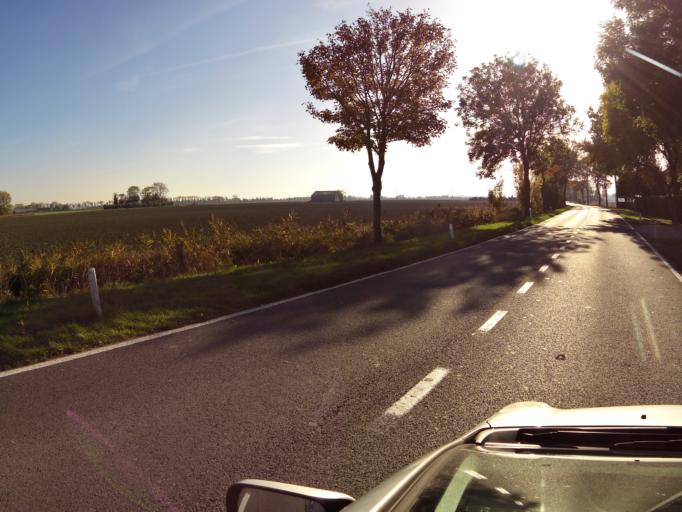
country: BE
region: Flanders
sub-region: Provincie West-Vlaanderen
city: Diksmuide
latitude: 51.1066
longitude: 2.8375
